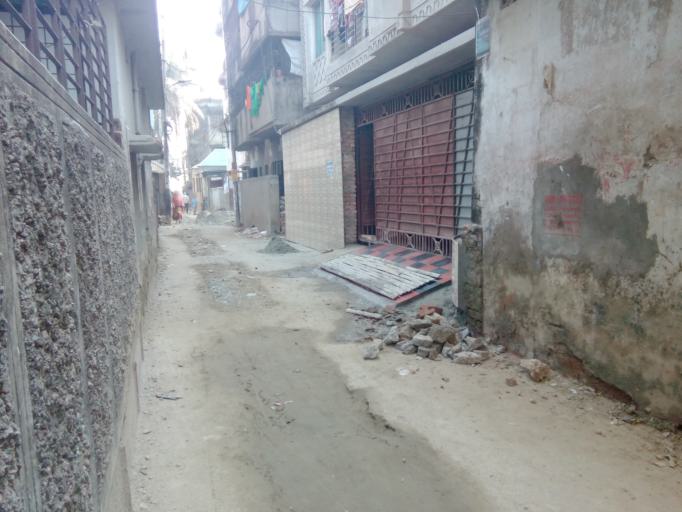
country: BD
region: Dhaka
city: Paltan
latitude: 23.7466
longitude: 90.4186
